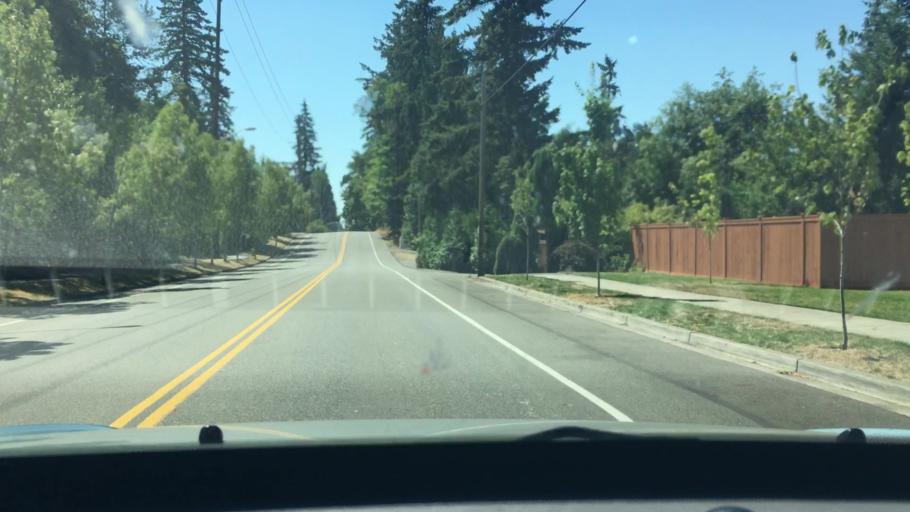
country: US
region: Washington
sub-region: King County
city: Newcastle
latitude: 47.5383
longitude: -122.1857
